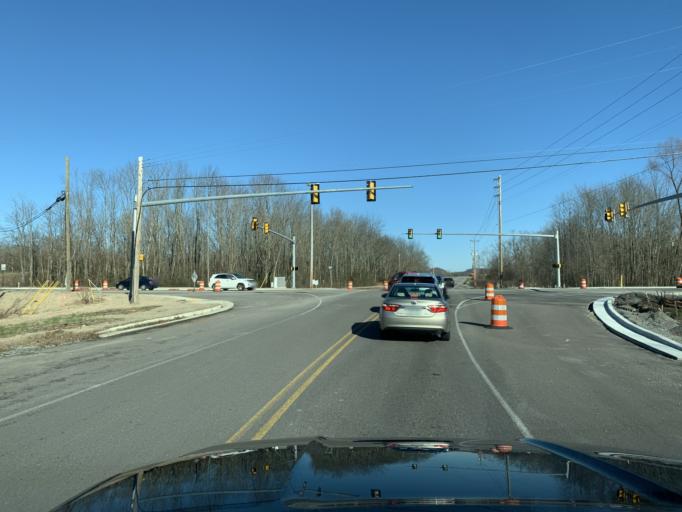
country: US
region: Tennessee
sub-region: Maury County
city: Spring Hill
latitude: 35.7521
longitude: -86.9219
